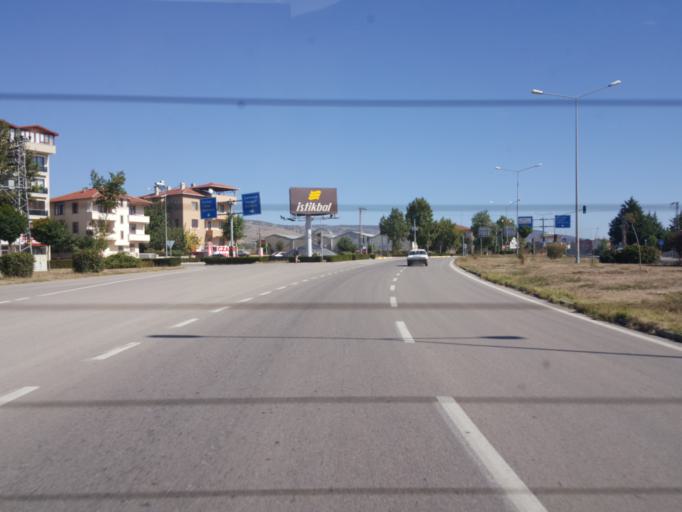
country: TR
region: Tokat
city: Zile
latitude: 40.3080
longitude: 35.9016
